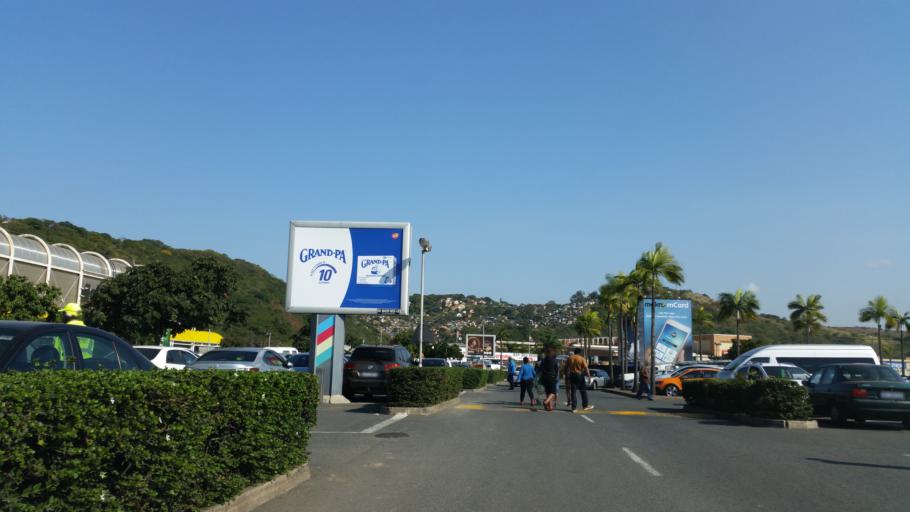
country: ZA
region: KwaZulu-Natal
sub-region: eThekwini Metropolitan Municipality
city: Berea
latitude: -29.8136
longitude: 30.9938
